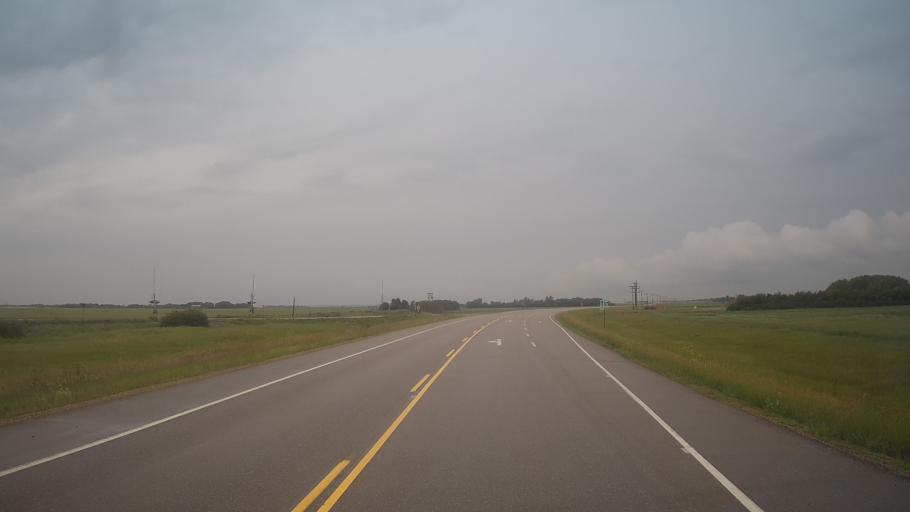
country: CA
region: Saskatchewan
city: Wilkie
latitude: 52.3108
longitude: -108.6913
